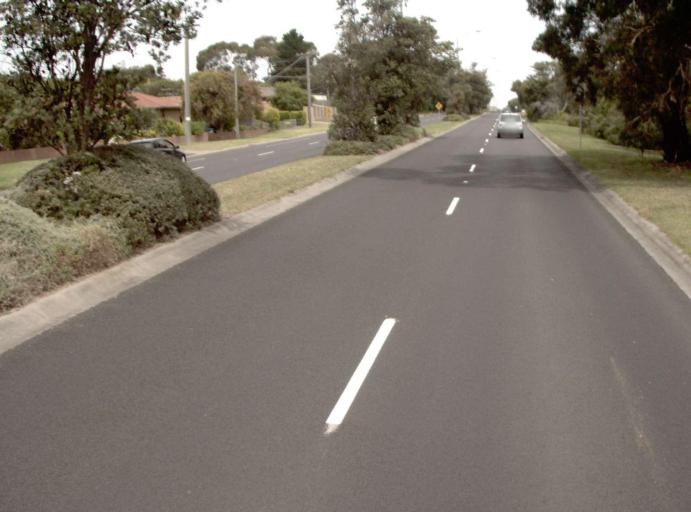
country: AU
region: Victoria
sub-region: Mornington Peninsula
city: Rosebud West
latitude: -38.3732
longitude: 144.8891
